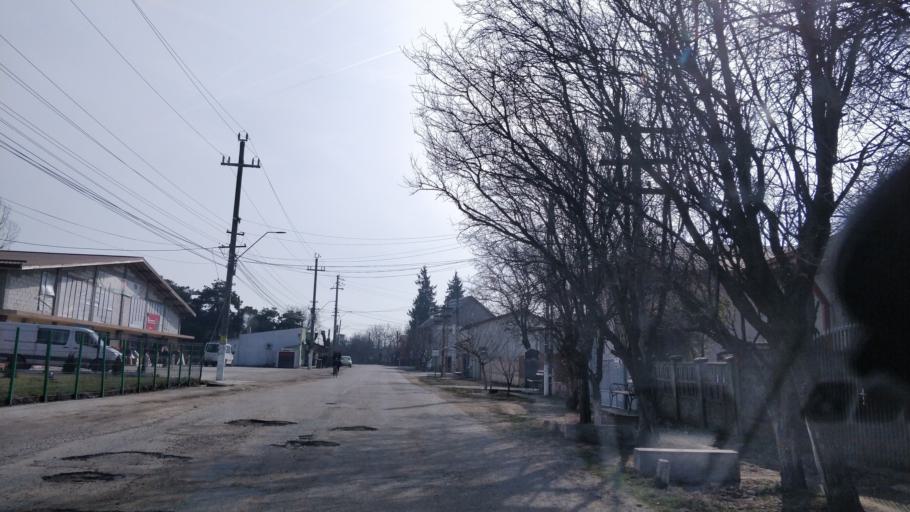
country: RO
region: Giurgiu
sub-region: Comuna Ulmi
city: Ulmi
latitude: 44.4711
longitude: 25.7667
